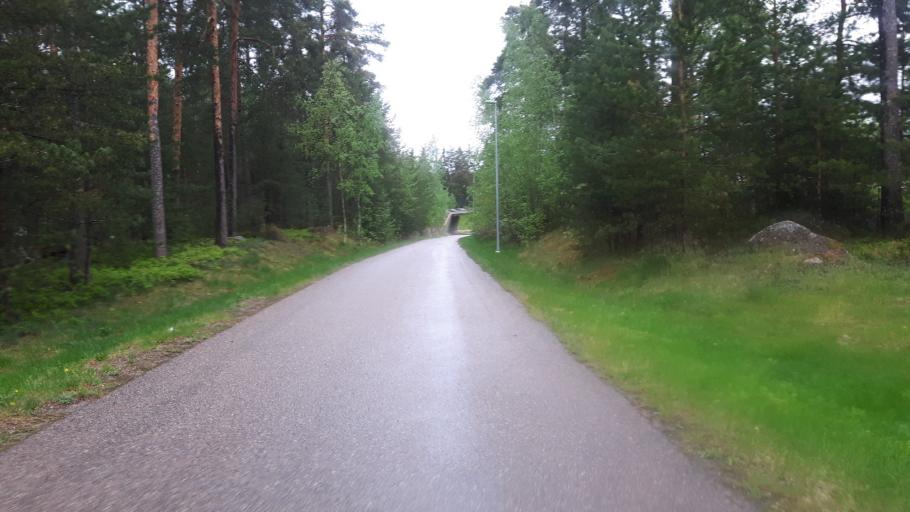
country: FI
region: Kymenlaakso
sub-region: Kotka-Hamina
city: Karhula
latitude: 60.5319
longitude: 26.9546
